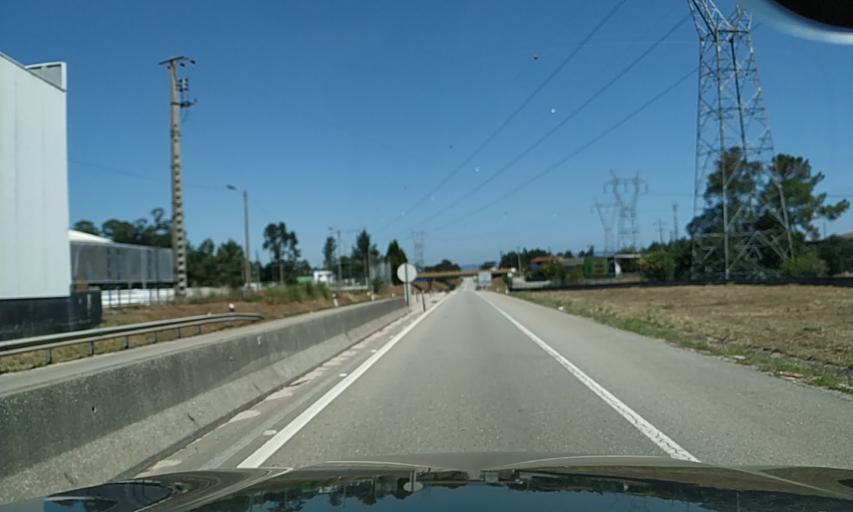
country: PT
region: Aveiro
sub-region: Agueda
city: Agueda
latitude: 40.5783
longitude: -8.4740
